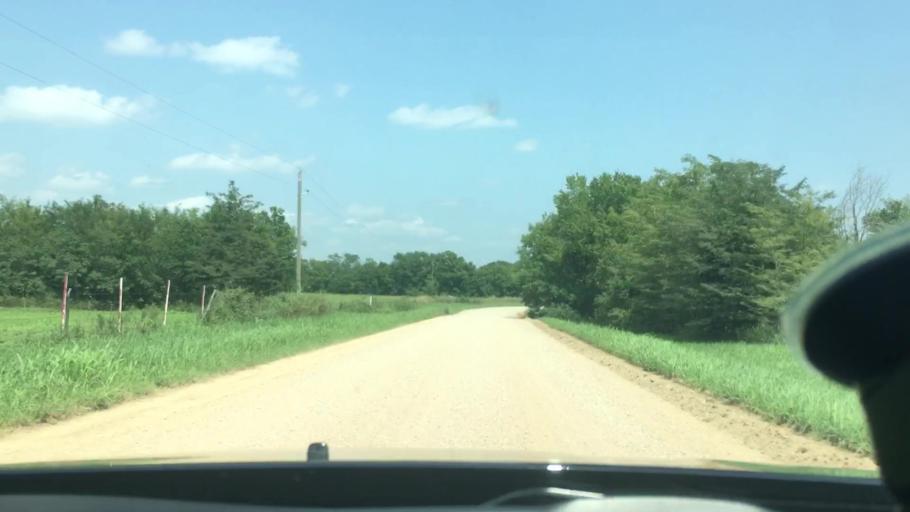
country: US
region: Oklahoma
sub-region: Coal County
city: Coalgate
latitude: 34.4323
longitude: -96.4502
